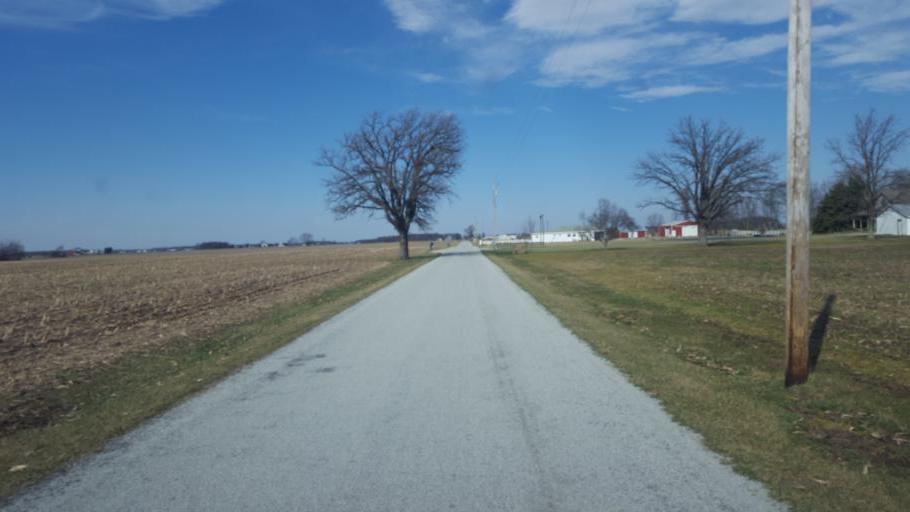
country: US
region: Ohio
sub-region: Hardin County
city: Kenton
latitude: 40.6477
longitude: -83.4959
